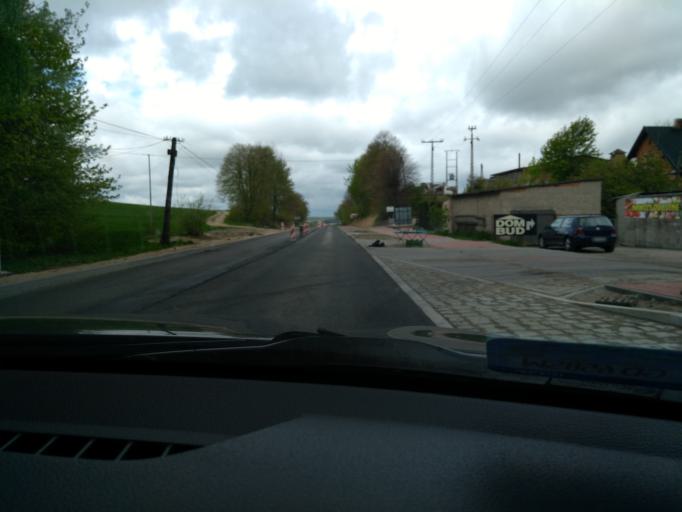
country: PL
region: Pomeranian Voivodeship
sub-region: Powiat kartuski
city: Kartuzy
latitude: 54.3449
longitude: 18.1564
